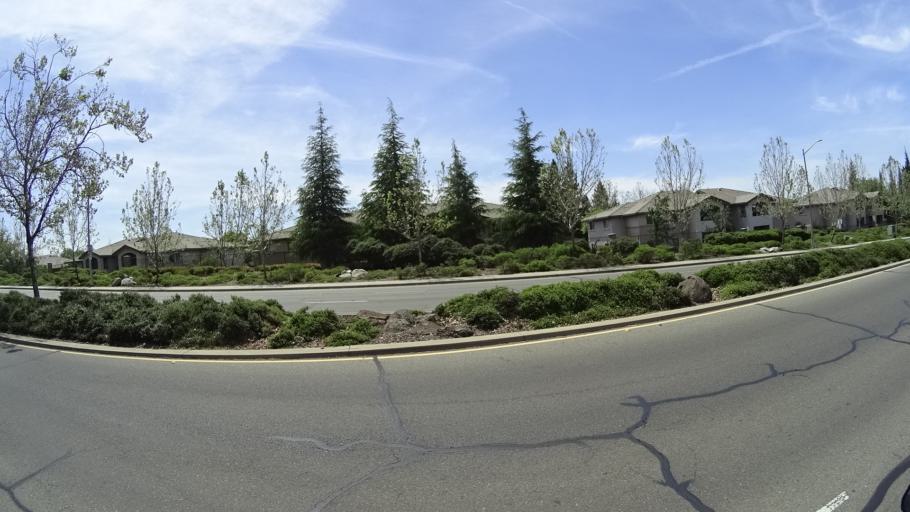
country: US
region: California
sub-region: Placer County
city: Rocklin
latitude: 38.8081
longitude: -121.2785
